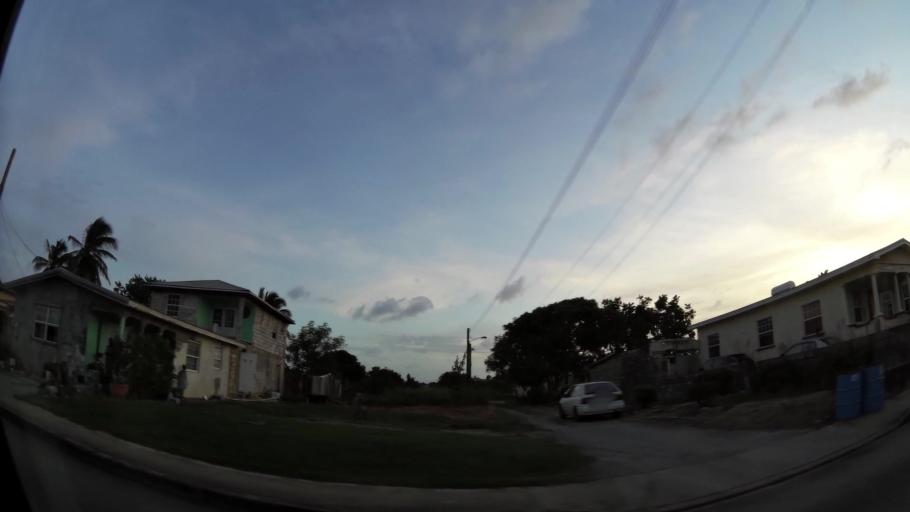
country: BB
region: Saint Philip
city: Crane
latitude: 13.1047
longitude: -59.4615
